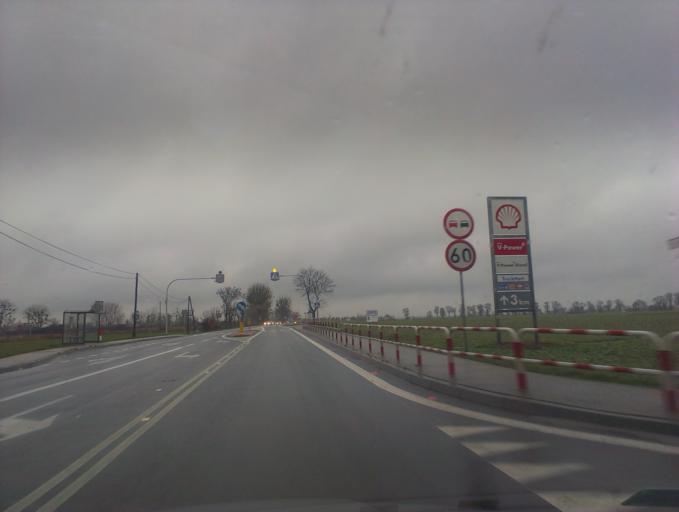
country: PL
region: Greater Poland Voivodeship
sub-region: Powiat obornicki
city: Oborniki
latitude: 52.5933
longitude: 16.8251
